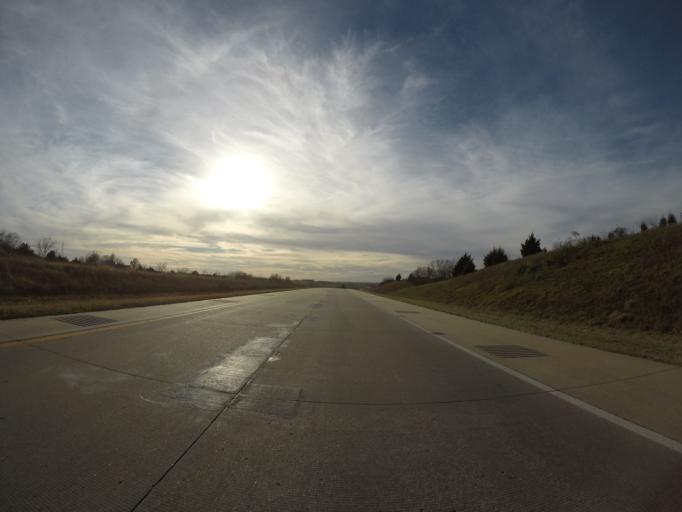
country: US
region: Kansas
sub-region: Franklin County
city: Ottawa
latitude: 38.5632
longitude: -95.3112
